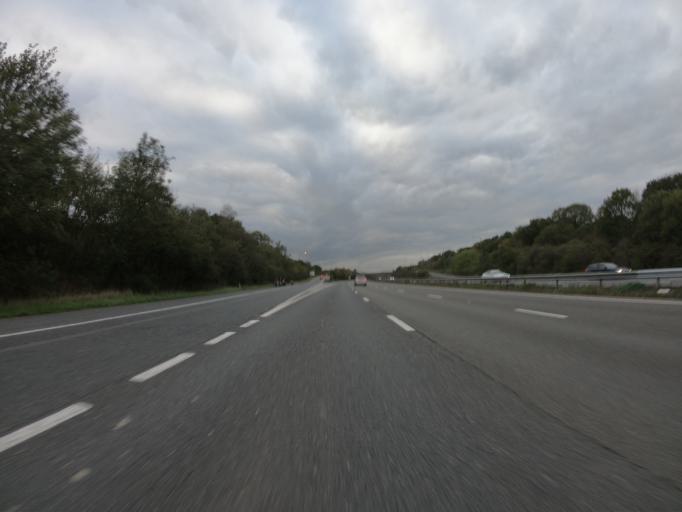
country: GB
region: England
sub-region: Greater London
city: Bexley
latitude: 51.4343
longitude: 0.1829
